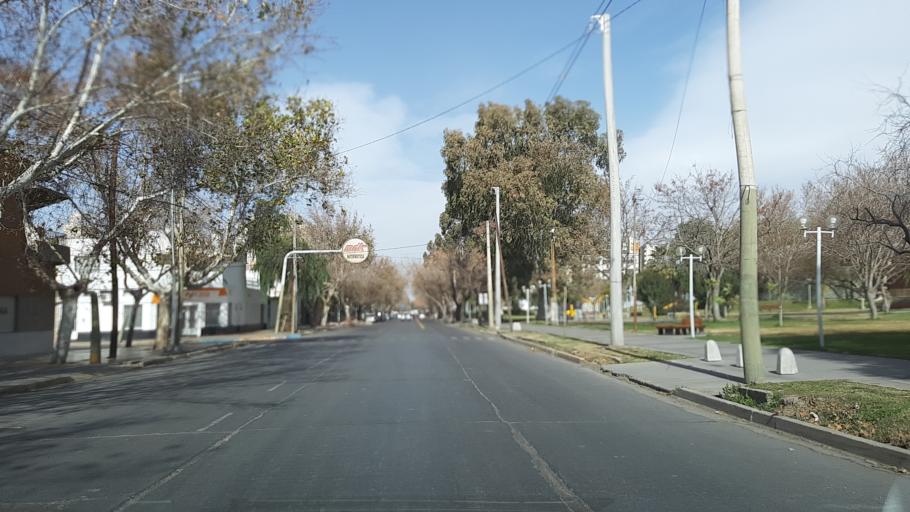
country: AR
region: San Juan
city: San Juan
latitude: -31.5321
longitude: -68.5370
